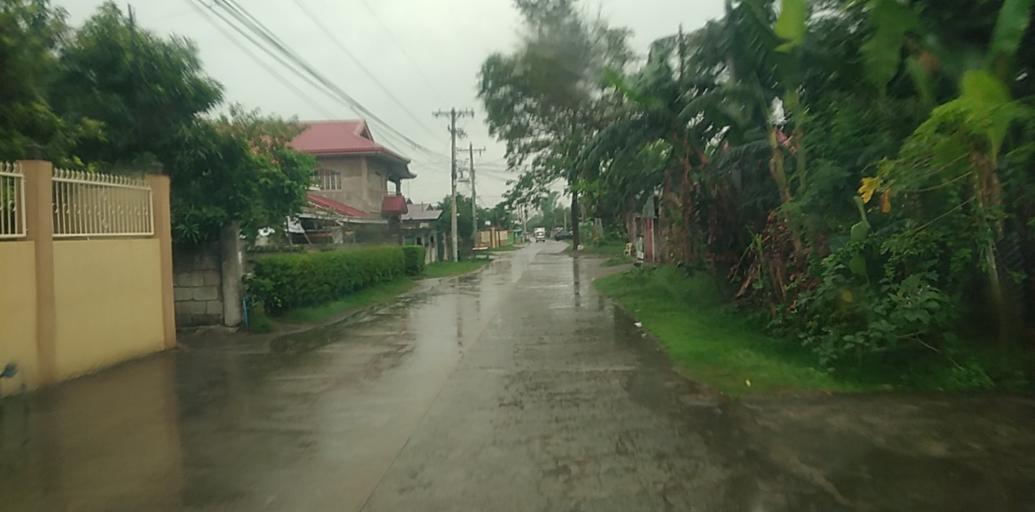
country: PH
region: Central Luzon
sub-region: Province of Pampanga
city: Arenas
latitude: 15.1724
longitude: 120.6837
